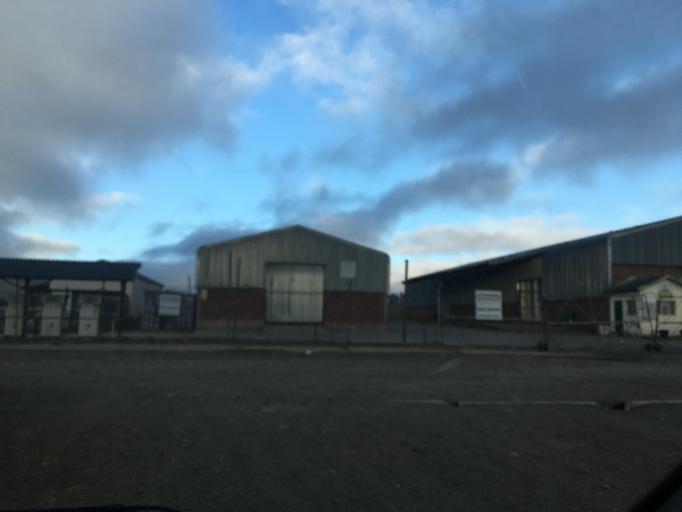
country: ZA
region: Eastern Cape
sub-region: Chris Hani District Municipality
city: Elliot
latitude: -31.3360
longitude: 27.8468
